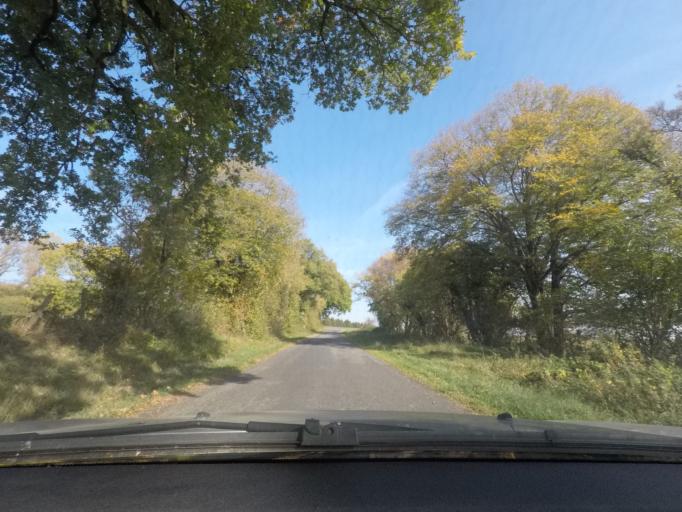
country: BE
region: Wallonia
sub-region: Province du Luxembourg
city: Tintigny
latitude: 49.6945
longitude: 5.4591
